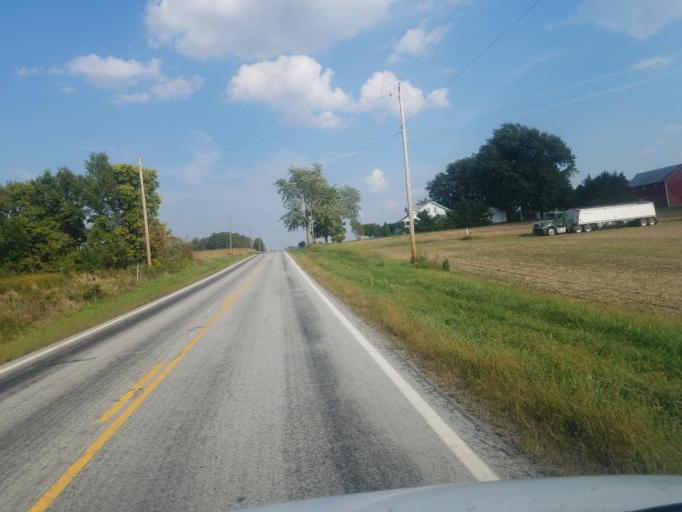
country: US
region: Ohio
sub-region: Hardin County
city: Forest
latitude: 40.8910
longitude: -83.5480
